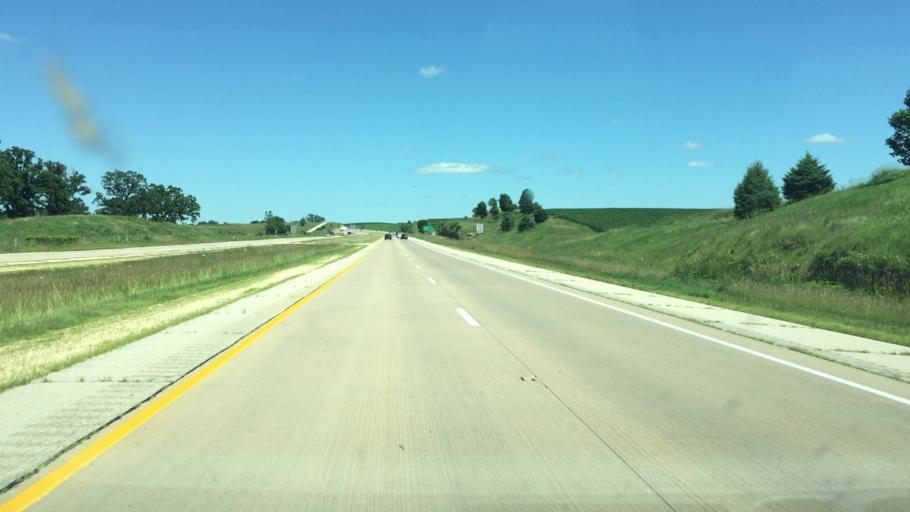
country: US
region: Wisconsin
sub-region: Grant County
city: Platteville
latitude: 42.7372
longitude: -90.4229
